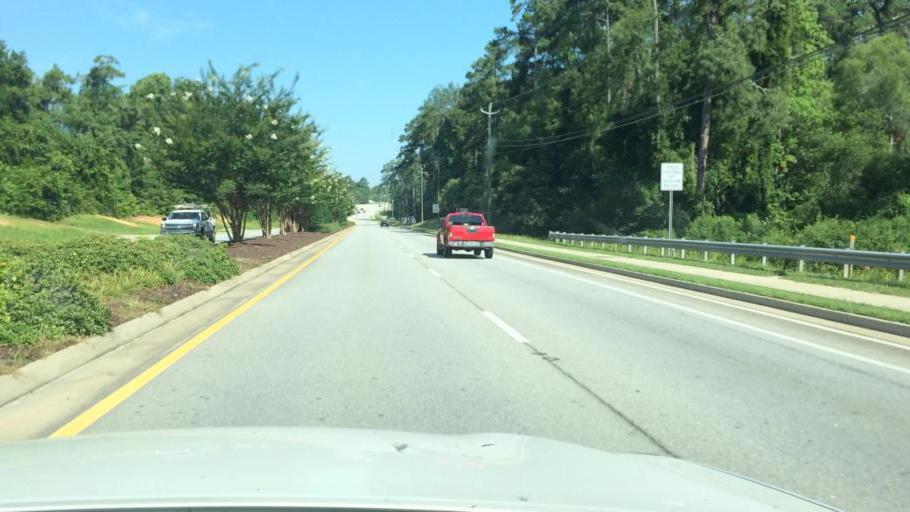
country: US
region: Georgia
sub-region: Columbia County
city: Martinez
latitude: 33.5207
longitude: -82.0640
